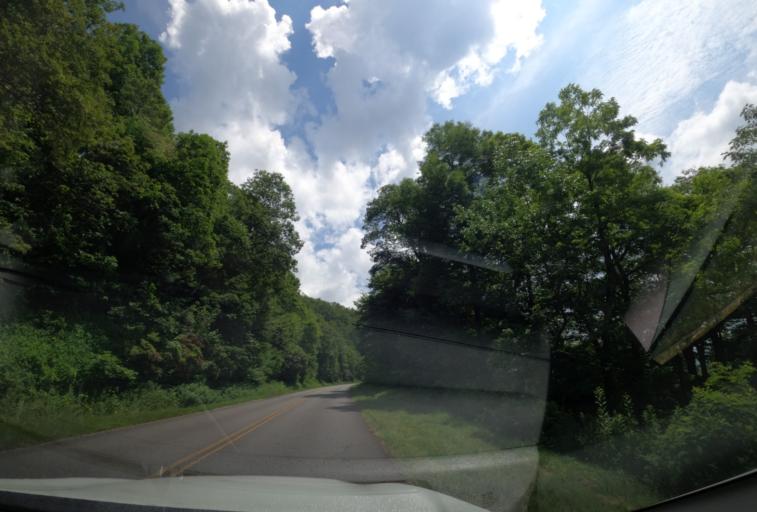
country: US
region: North Carolina
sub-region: Transylvania County
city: Brevard
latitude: 35.3566
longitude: -82.7983
